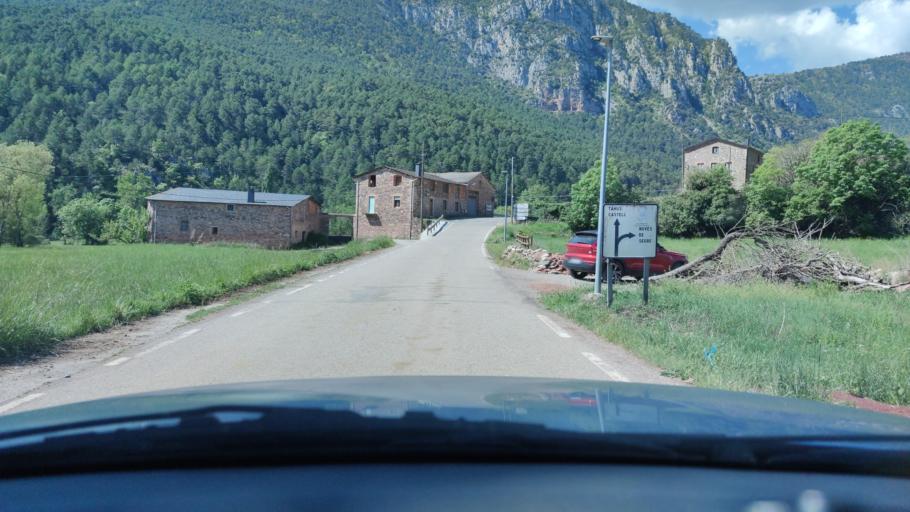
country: ES
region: Catalonia
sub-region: Provincia de Lleida
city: Coll de Nargo
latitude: 42.2938
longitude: 1.3459
